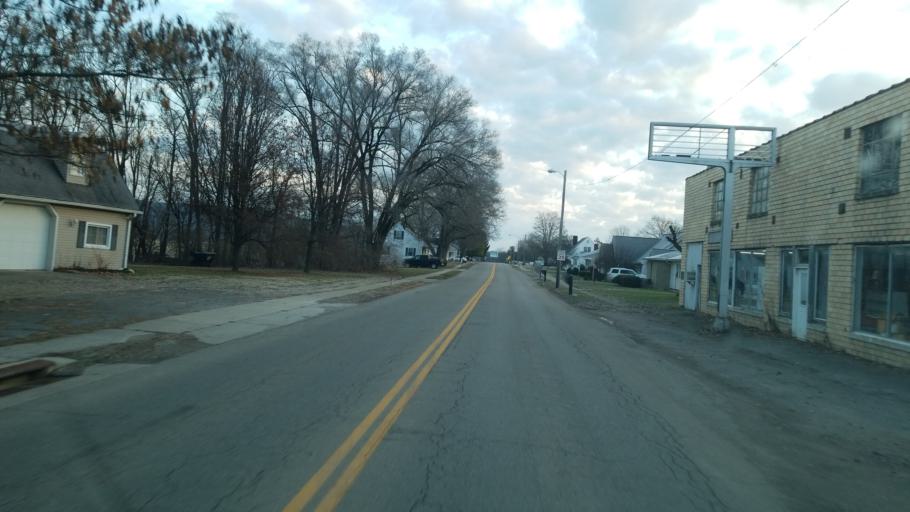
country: US
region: Ohio
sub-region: Highland County
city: Greenfield
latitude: 39.2289
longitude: -83.2643
